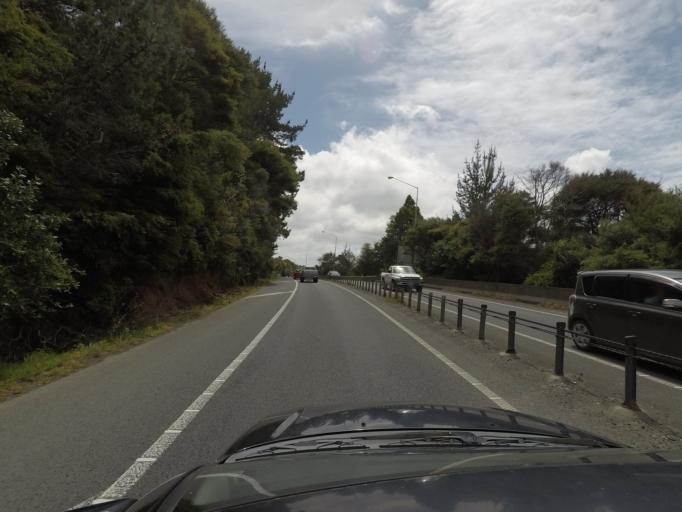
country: NZ
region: Auckland
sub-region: Auckland
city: Warkworth
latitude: -36.5255
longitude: 174.6775
